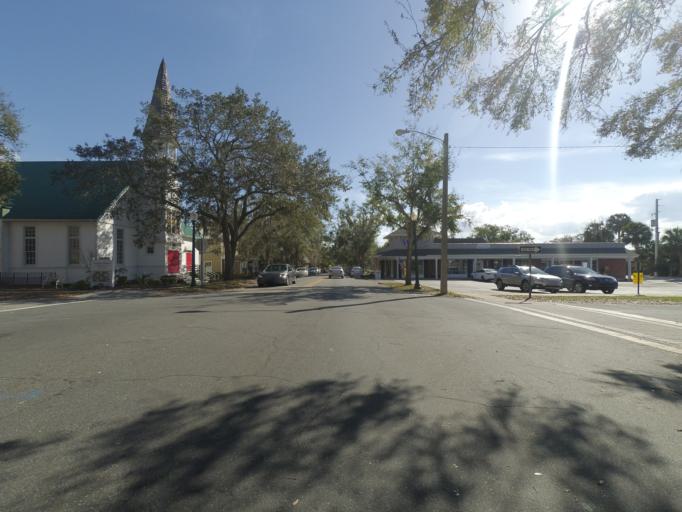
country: US
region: Florida
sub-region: Lake County
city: Mount Dora
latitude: 28.8024
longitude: -81.6448
